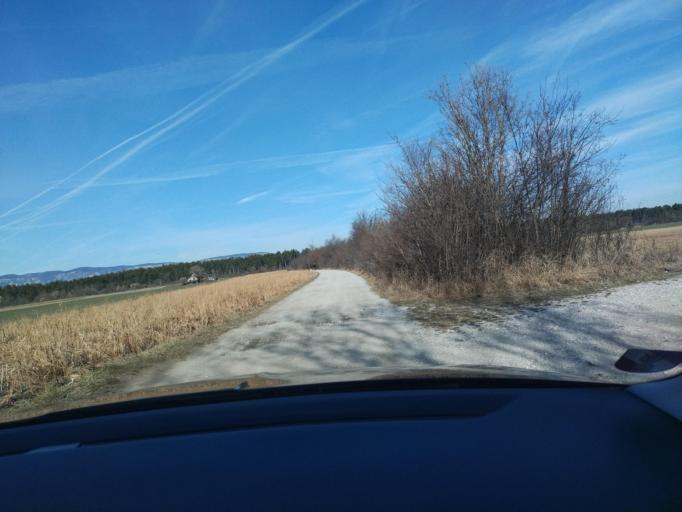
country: AT
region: Lower Austria
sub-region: Politischer Bezirk Neunkirchen
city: Breitenau
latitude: 47.7408
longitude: 16.1675
